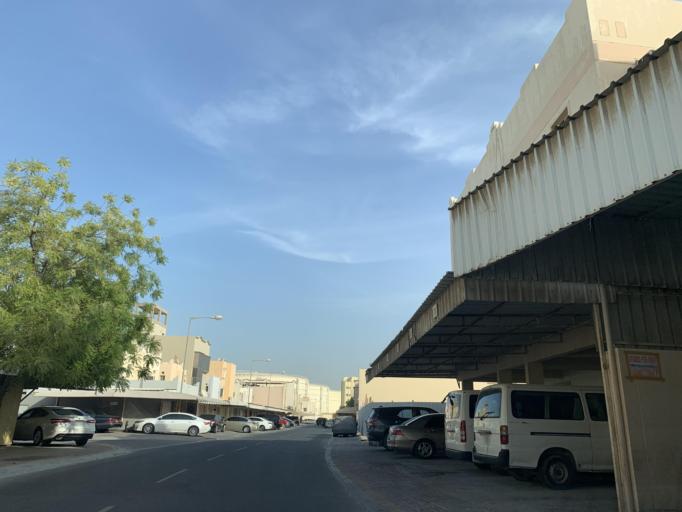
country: BH
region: Northern
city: Ar Rifa'
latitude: 26.1285
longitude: 50.5820
